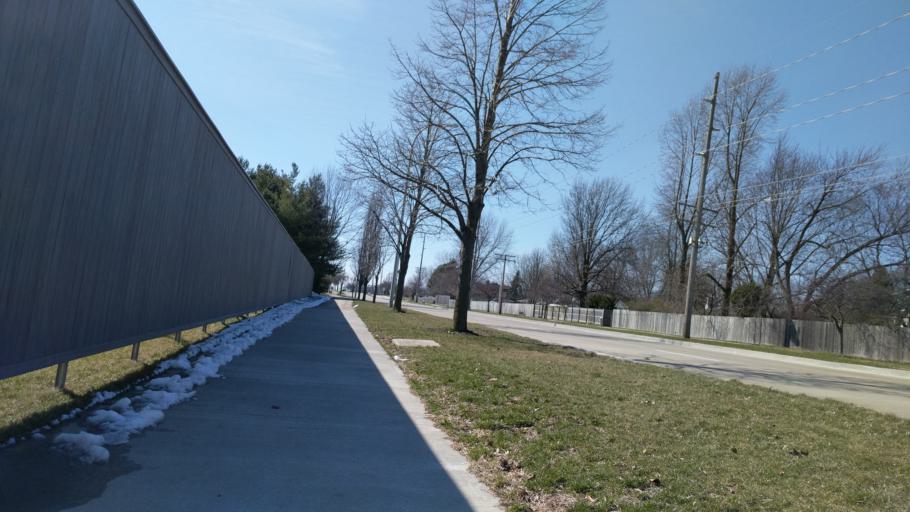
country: US
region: Illinois
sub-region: Champaign County
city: Urbana
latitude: 40.0838
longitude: -88.2050
